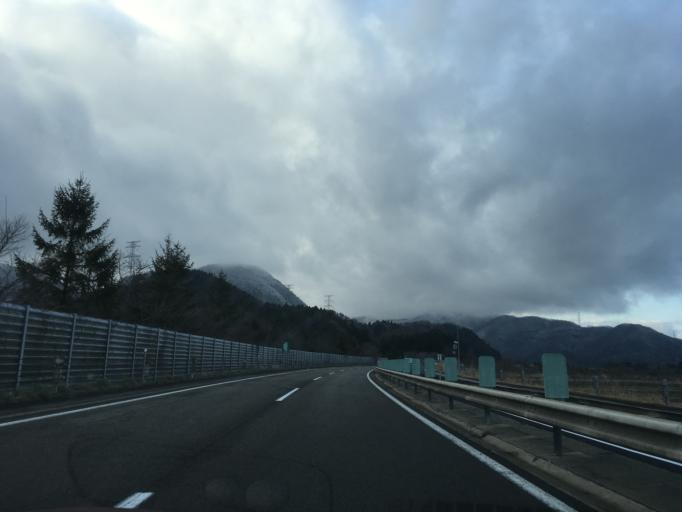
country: JP
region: Miyagi
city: Shiroishi
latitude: 38.1855
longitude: 140.5998
